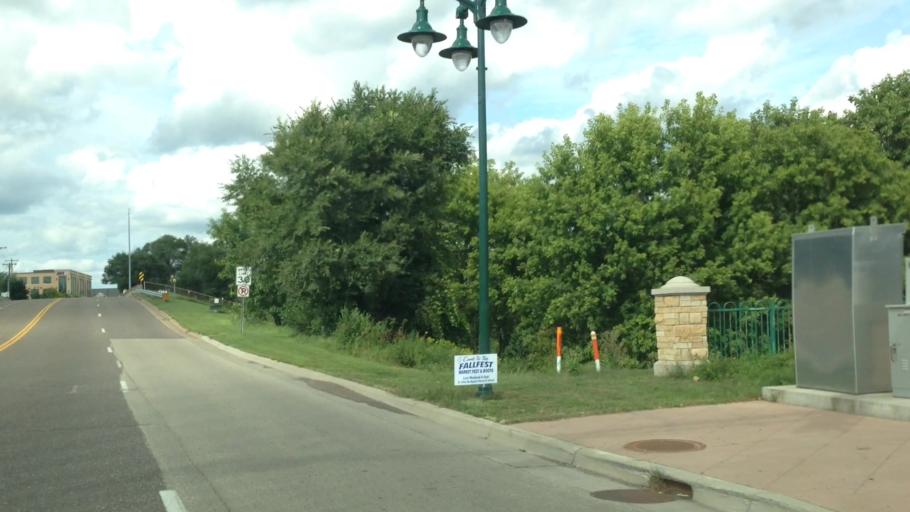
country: US
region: Minnesota
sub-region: Ramsey County
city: New Brighton
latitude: 45.0654
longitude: -93.1932
